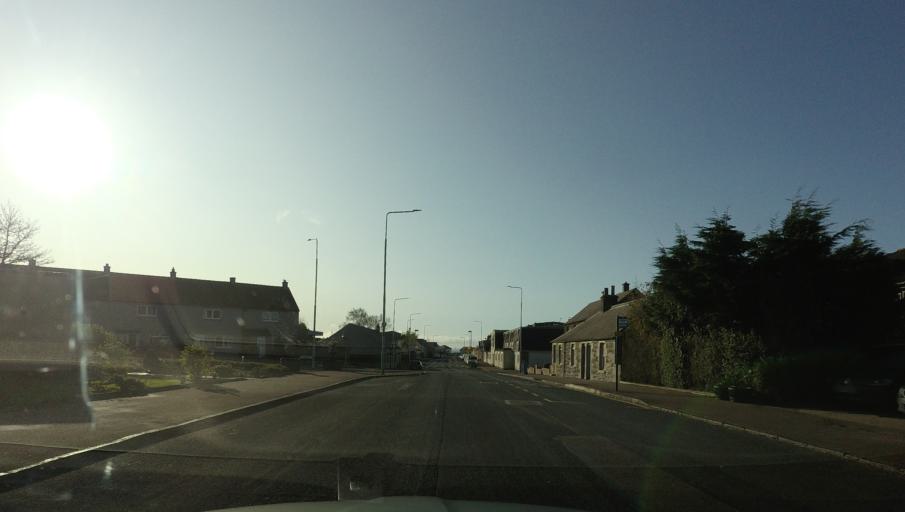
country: GB
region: Scotland
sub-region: Fife
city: Townhill
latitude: 56.0990
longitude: -3.4070
